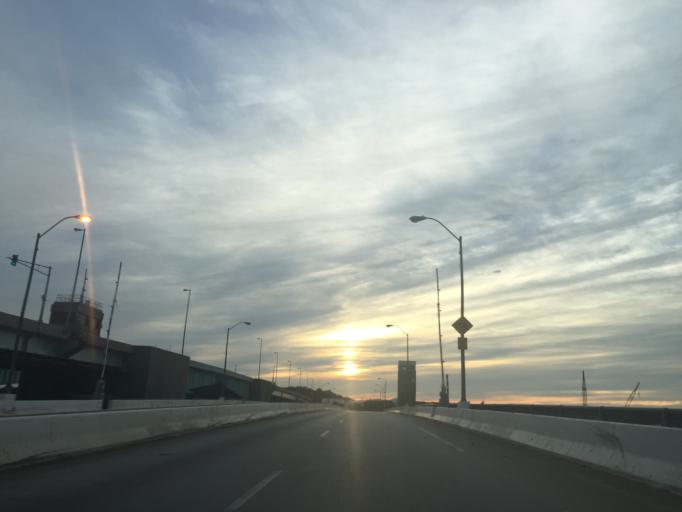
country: US
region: Maryland
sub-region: Anne Arundel County
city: Brooklyn Park
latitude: 39.2078
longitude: -76.5790
